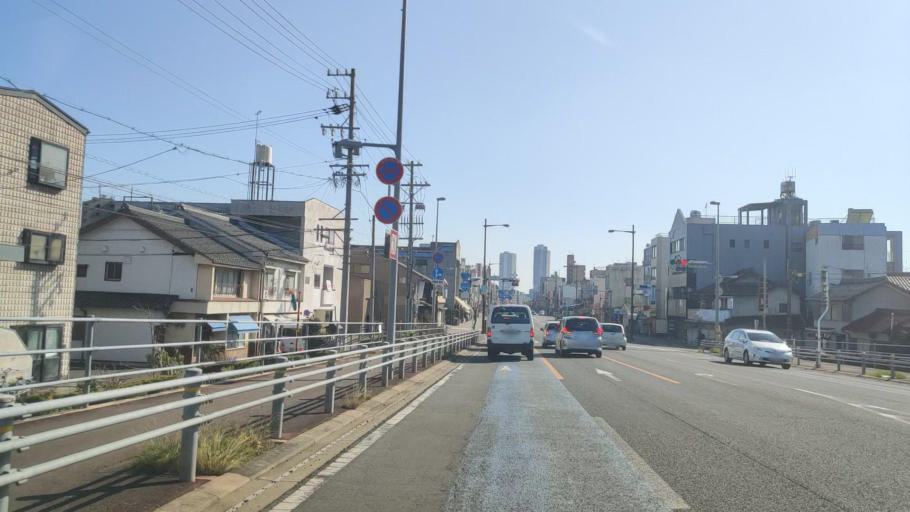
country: JP
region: Gifu
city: Gifu-shi
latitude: 35.4269
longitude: 136.7511
